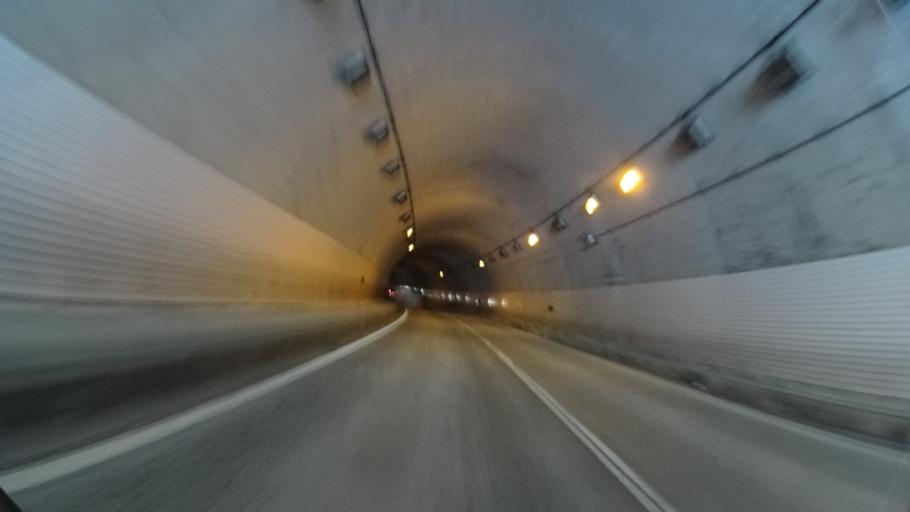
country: JP
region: Ehime
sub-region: Nishiuwa-gun
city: Ikata-cho
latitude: 33.5367
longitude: 132.4074
